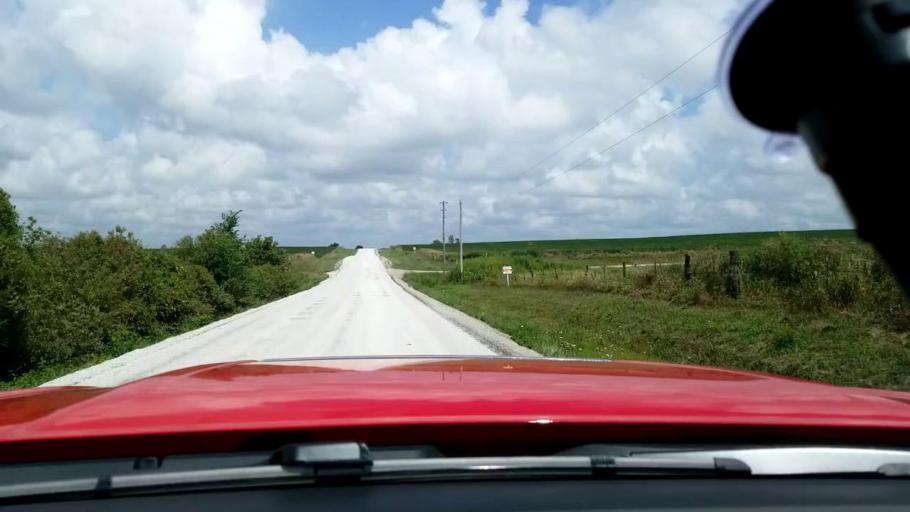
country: US
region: Iowa
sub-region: Decatur County
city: Lamoni
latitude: 40.6664
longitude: -94.0483
